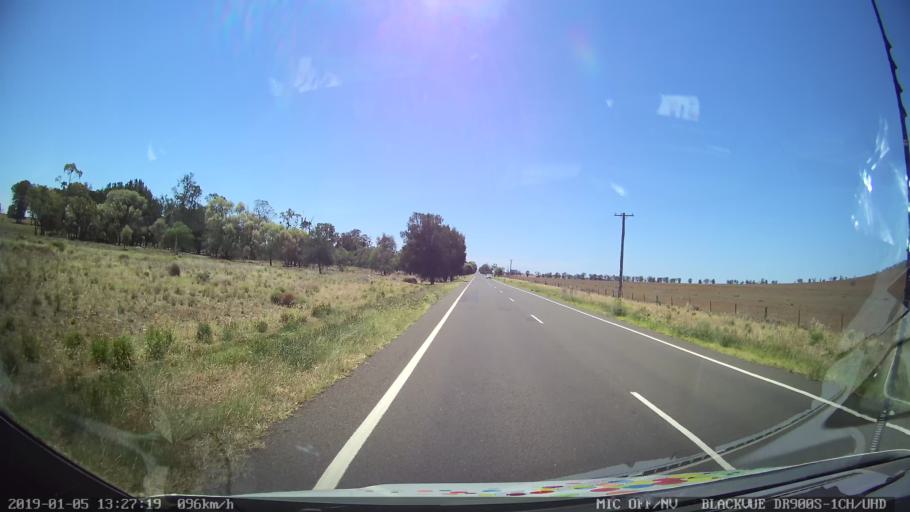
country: AU
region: New South Wales
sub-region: Gunnedah
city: Gunnedah
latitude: -31.0455
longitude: 150.0277
